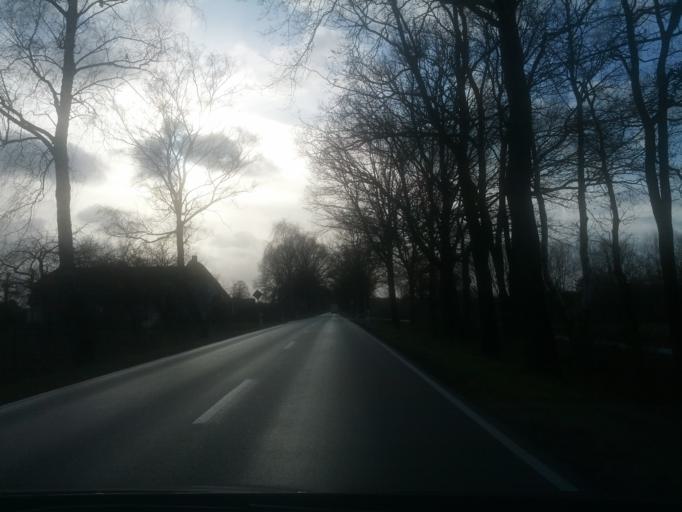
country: DE
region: Lower Saxony
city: Helvesiek
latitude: 53.2313
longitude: 9.4844
